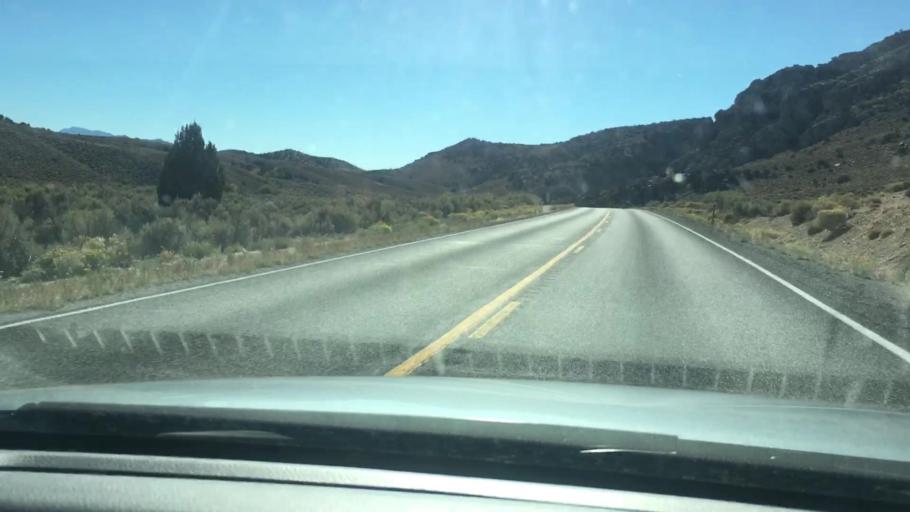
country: US
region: Nevada
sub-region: White Pine County
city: Ely
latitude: 38.8035
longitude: -115.3796
